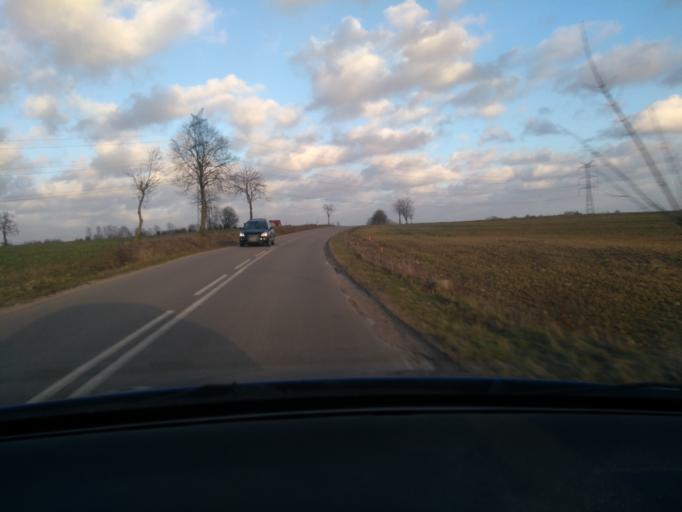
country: PL
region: Pomeranian Voivodeship
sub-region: Powiat kartuski
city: Przodkowo
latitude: 54.4171
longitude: 18.2927
